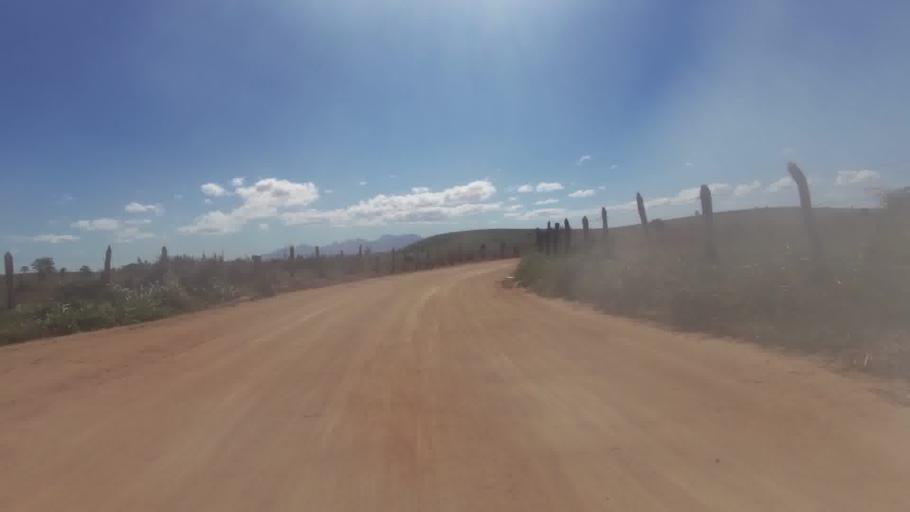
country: BR
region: Espirito Santo
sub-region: Marataizes
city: Marataizes
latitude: -21.1412
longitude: -40.9909
